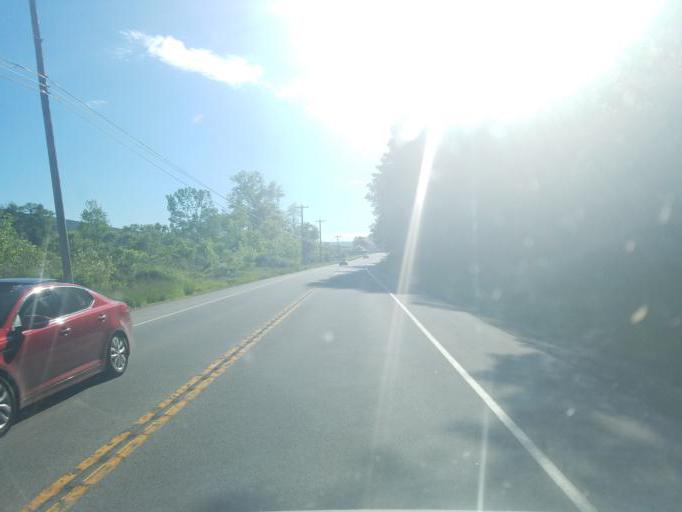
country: US
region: New York
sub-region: Herkimer County
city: Little Falls
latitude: 43.0231
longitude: -74.8960
